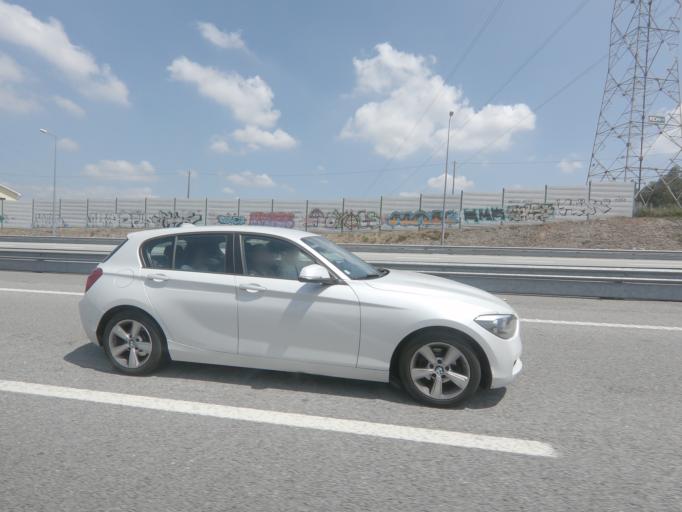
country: PT
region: Porto
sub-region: Valongo
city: Campo
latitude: 41.1808
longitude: -8.4461
